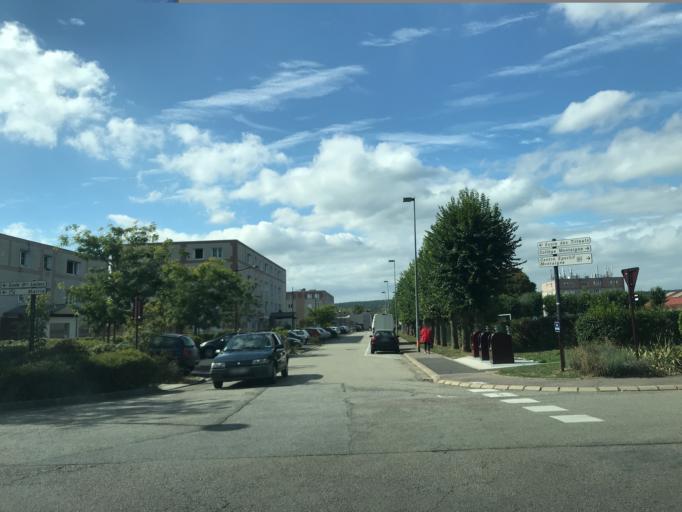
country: FR
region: Haute-Normandie
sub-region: Departement de l'Eure
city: Le Vaudreuil
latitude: 49.2578
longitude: 1.2085
